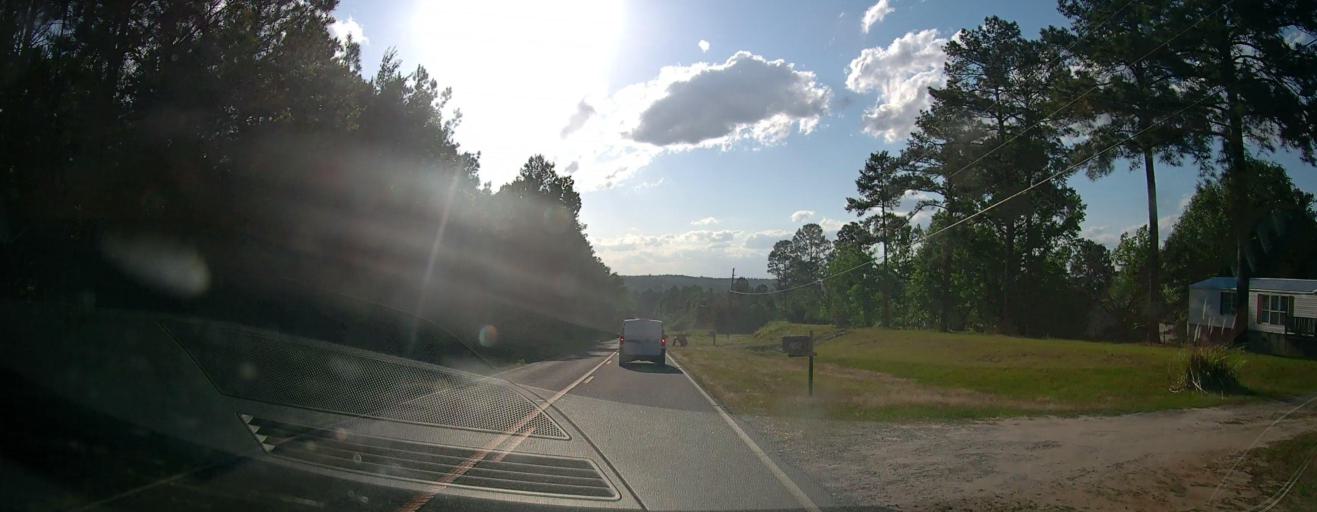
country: US
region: Georgia
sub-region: Peach County
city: Byron
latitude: 32.6764
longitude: -83.7689
